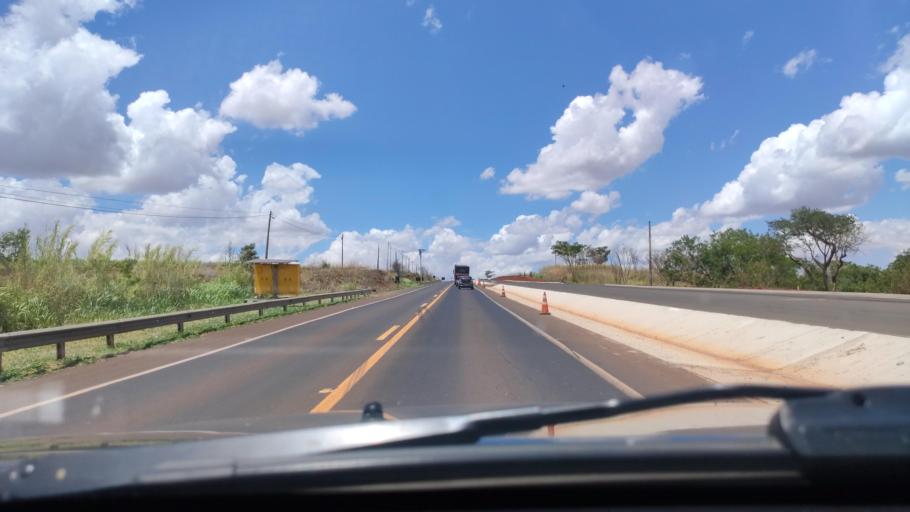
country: BR
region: Sao Paulo
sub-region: Jau
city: Jau
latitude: -22.2365
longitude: -48.5362
